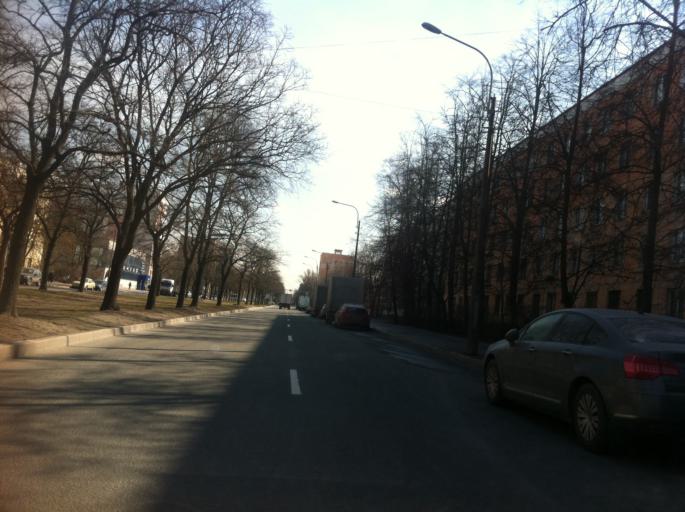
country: RU
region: St.-Petersburg
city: Dachnoye
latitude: 59.8453
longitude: 30.2613
